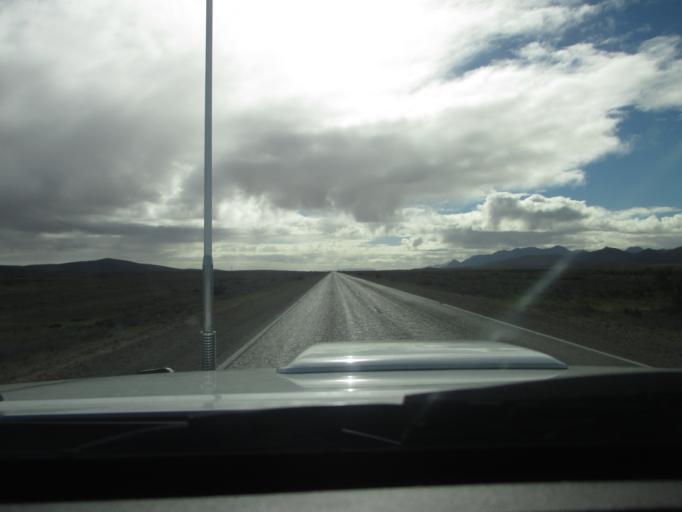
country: AU
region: South Australia
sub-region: Flinders Ranges
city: Quorn
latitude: -31.6616
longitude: 138.3747
